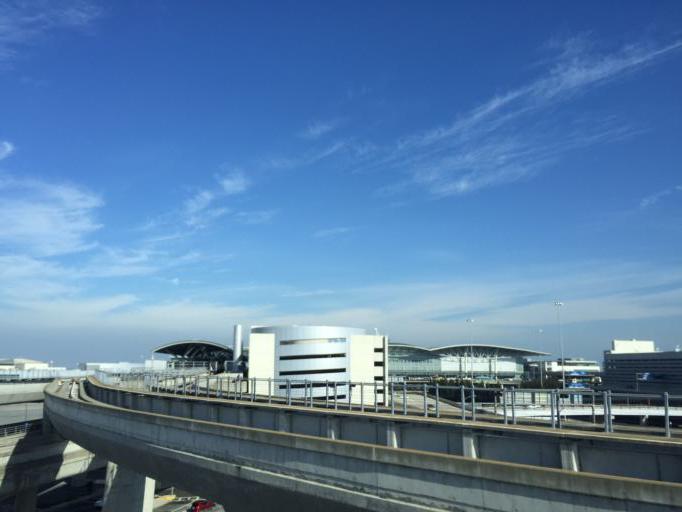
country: US
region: California
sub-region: San Mateo County
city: Millbrae
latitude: 37.6153
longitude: -122.3951
